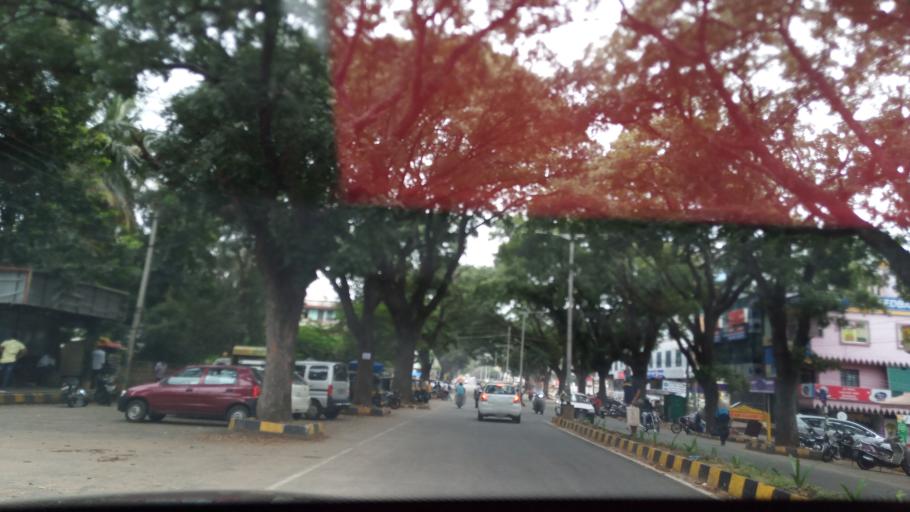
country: IN
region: Karnataka
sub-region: Mysore
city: Mysore
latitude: 12.3013
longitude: 76.6351
